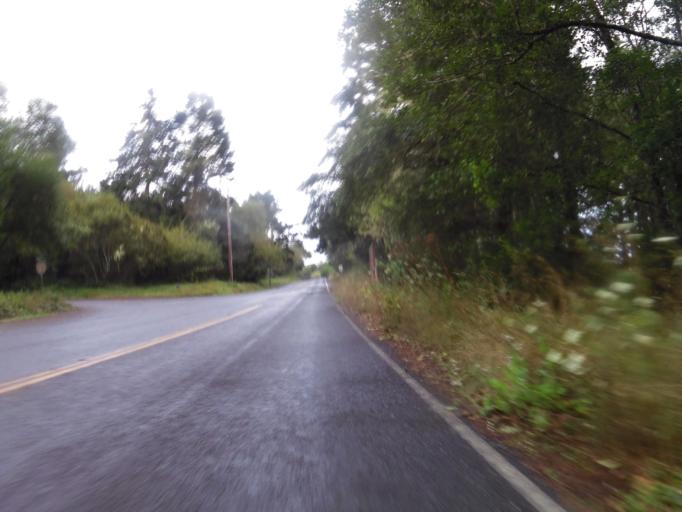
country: US
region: California
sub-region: Humboldt County
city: Westhaven-Moonstone
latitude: 41.0978
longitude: -124.1575
